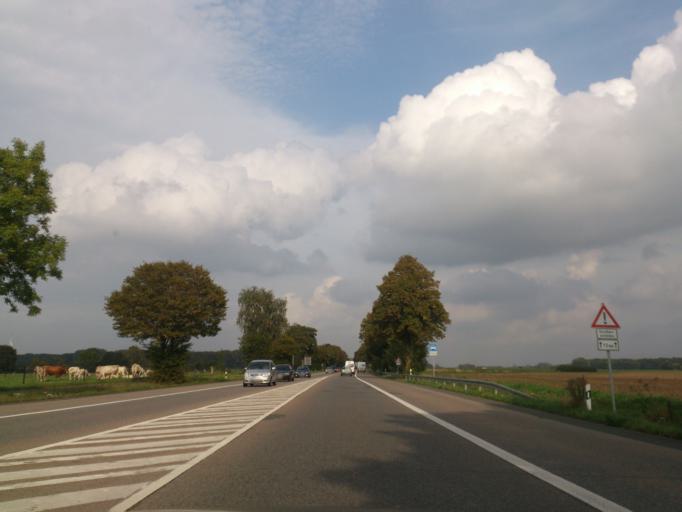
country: DE
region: North Rhine-Westphalia
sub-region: Regierungsbezirk Detmold
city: Salzkotten
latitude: 51.6788
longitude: 8.6282
